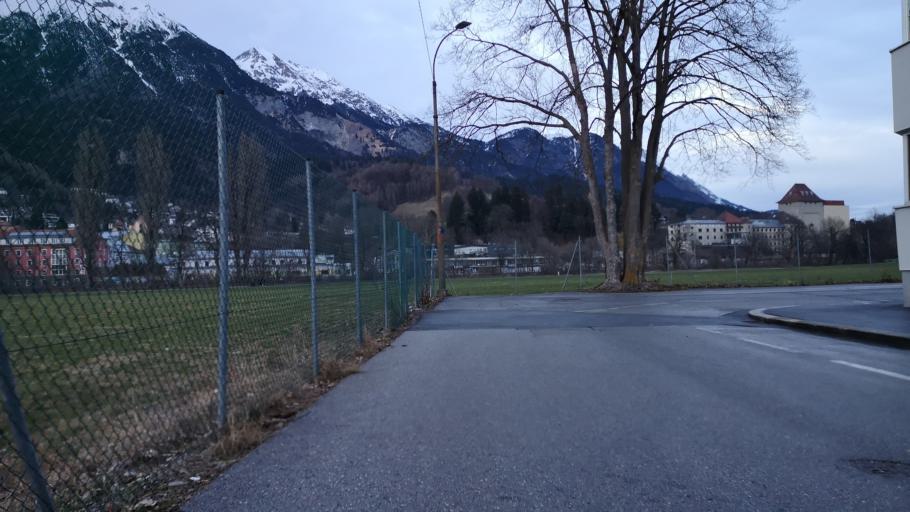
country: AT
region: Tyrol
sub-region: Innsbruck Stadt
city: Innsbruck
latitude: 47.2780
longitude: 11.4106
